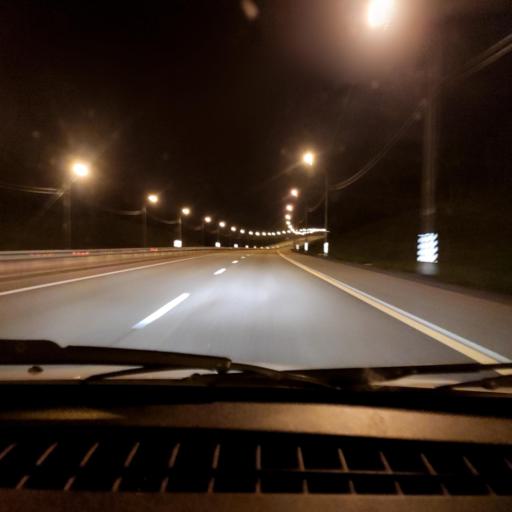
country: RU
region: Lipetsk
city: Zadonsk
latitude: 52.3890
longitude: 38.8662
